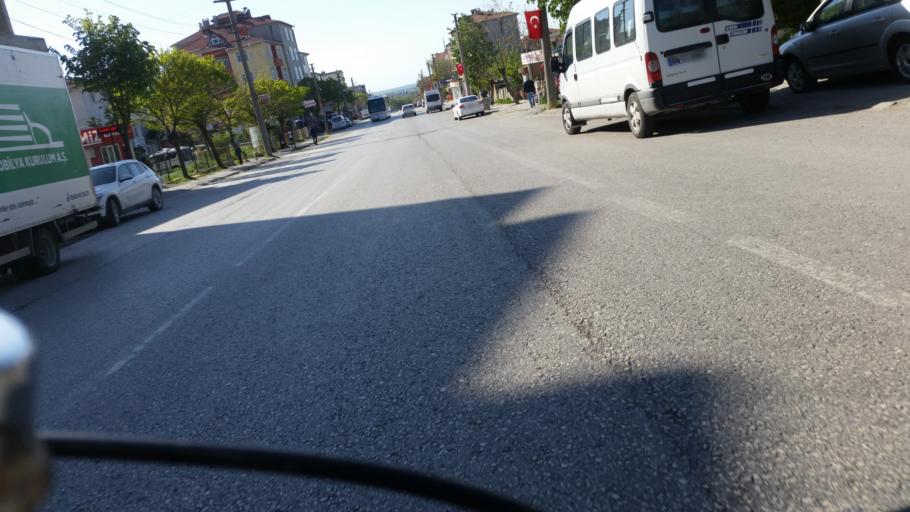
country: TR
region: Tekirdag
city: Cerkezkoey
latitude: 41.3578
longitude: 27.9507
